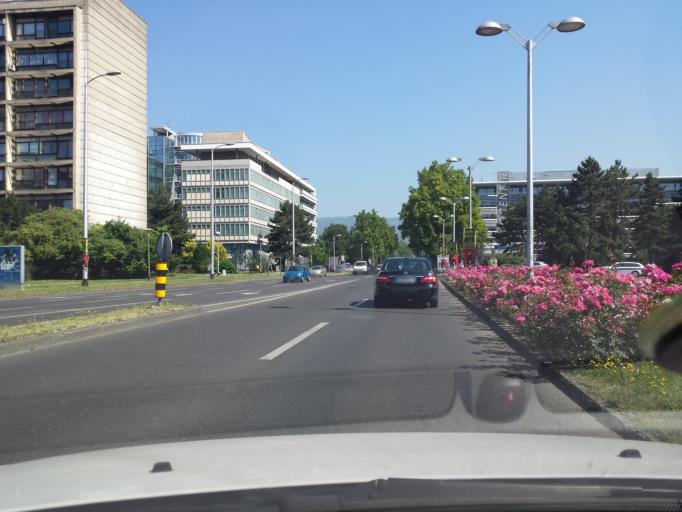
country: HR
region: Grad Zagreb
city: Zagreb - Centar
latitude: 45.8004
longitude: 15.9746
